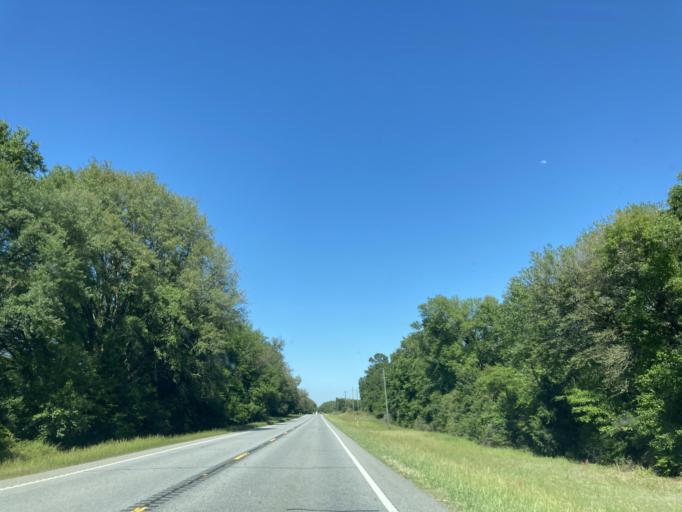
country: US
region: Georgia
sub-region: Baker County
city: Newton
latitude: 31.1964
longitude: -84.5090
